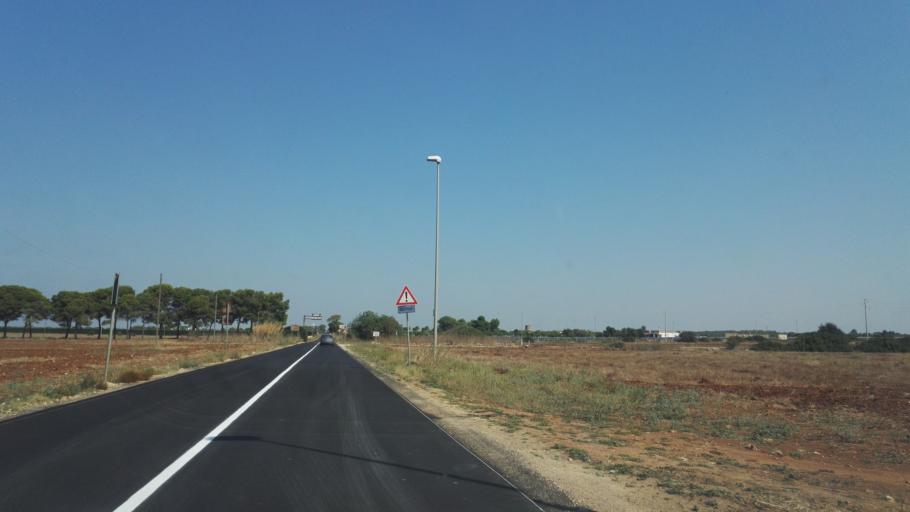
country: IT
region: Apulia
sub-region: Provincia di Lecce
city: Nardo
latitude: 40.2035
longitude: 17.9565
